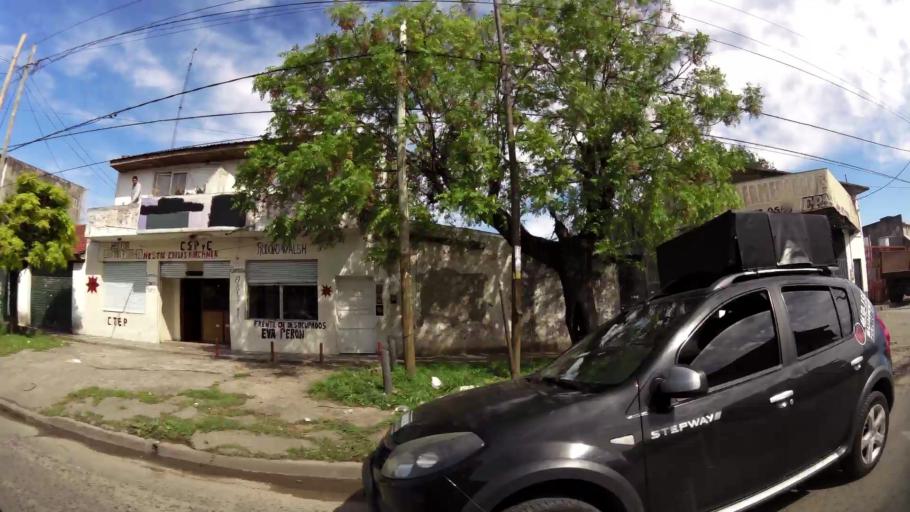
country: AR
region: Buenos Aires
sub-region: Partido de Quilmes
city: Quilmes
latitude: -34.7737
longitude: -58.3013
